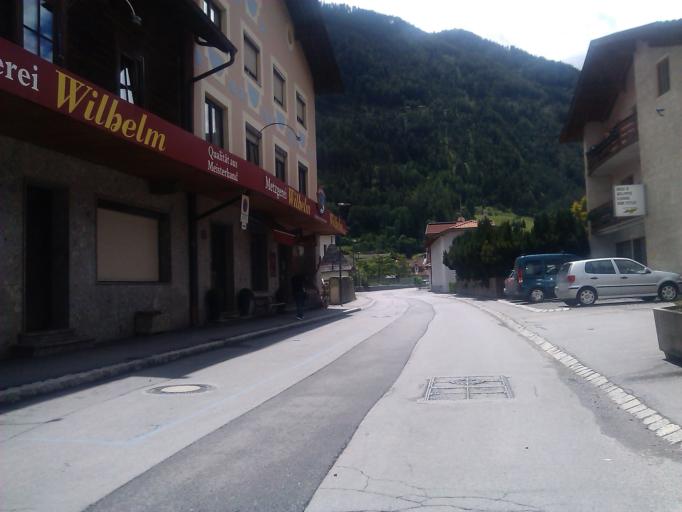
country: AT
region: Tyrol
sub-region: Politischer Bezirk Landeck
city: Prutz
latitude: 47.0750
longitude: 10.6644
